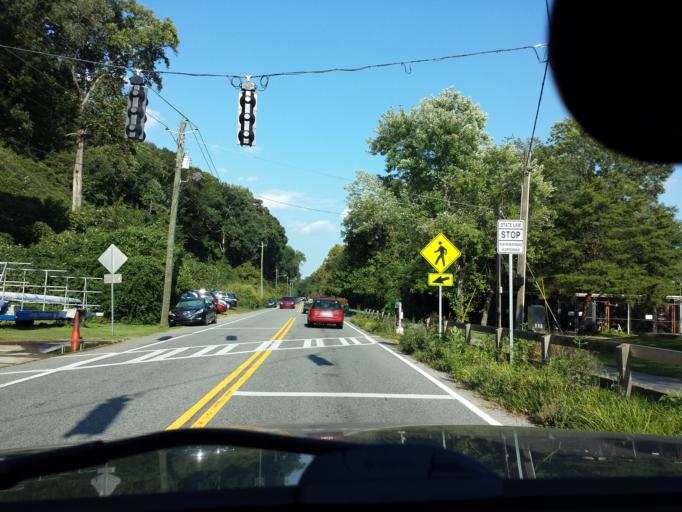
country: US
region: Georgia
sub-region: Fulton County
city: Roswell
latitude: 34.0024
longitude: -84.3624
